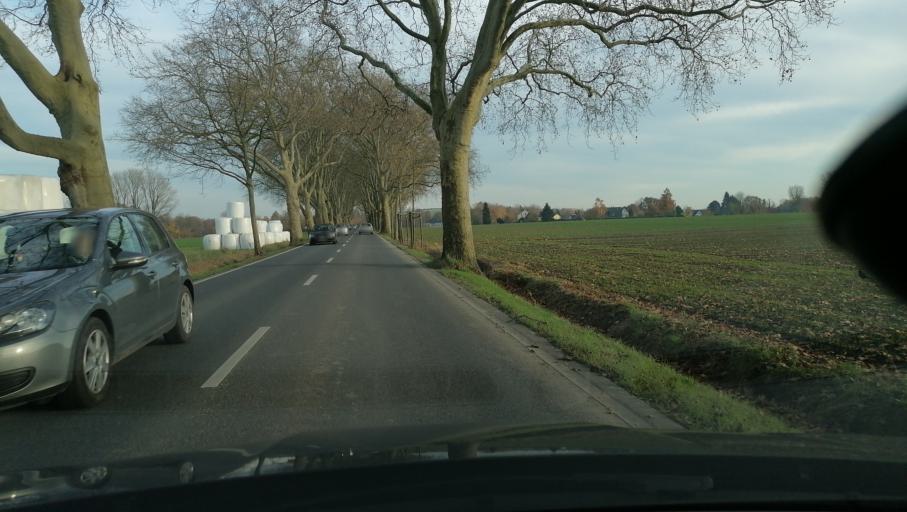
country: DE
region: North Rhine-Westphalia
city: Waltrop
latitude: 51.5505
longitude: 7.3902
